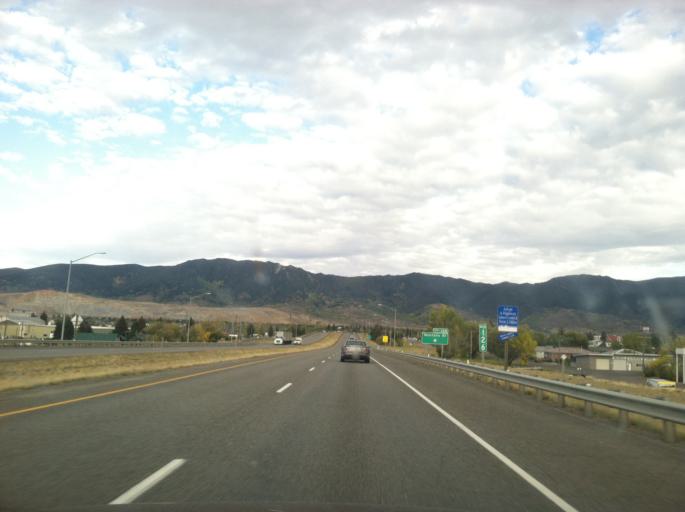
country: US
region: Montana
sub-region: Silver Bow County
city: Butte
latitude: 45.9924
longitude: -112.5460
